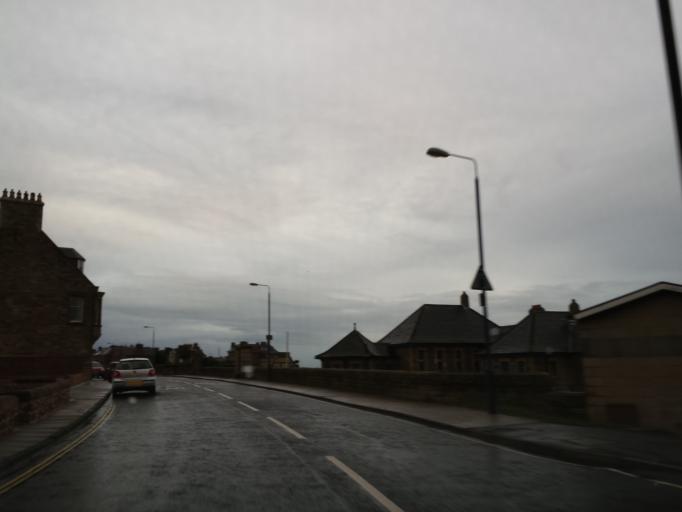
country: GB
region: Scotland
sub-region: East Lothian
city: Dunbar
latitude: 56.0038
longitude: -2.5182
